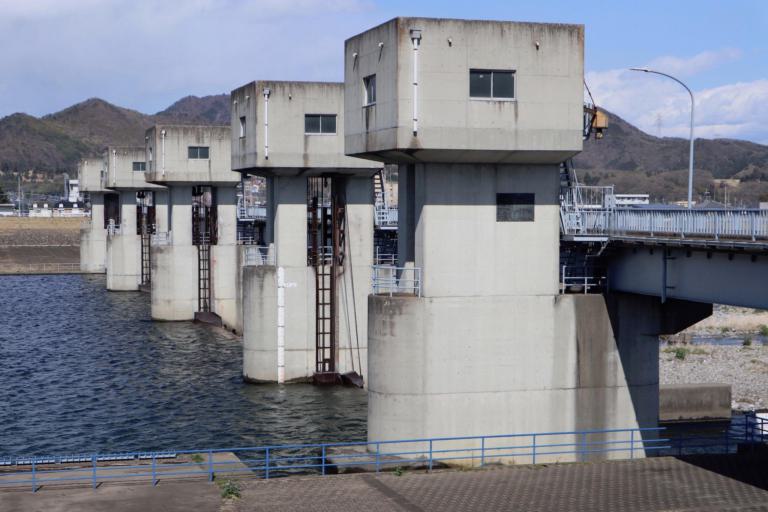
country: JP
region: Gunma
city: Kiryu
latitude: 36.3795
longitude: 139.3515
